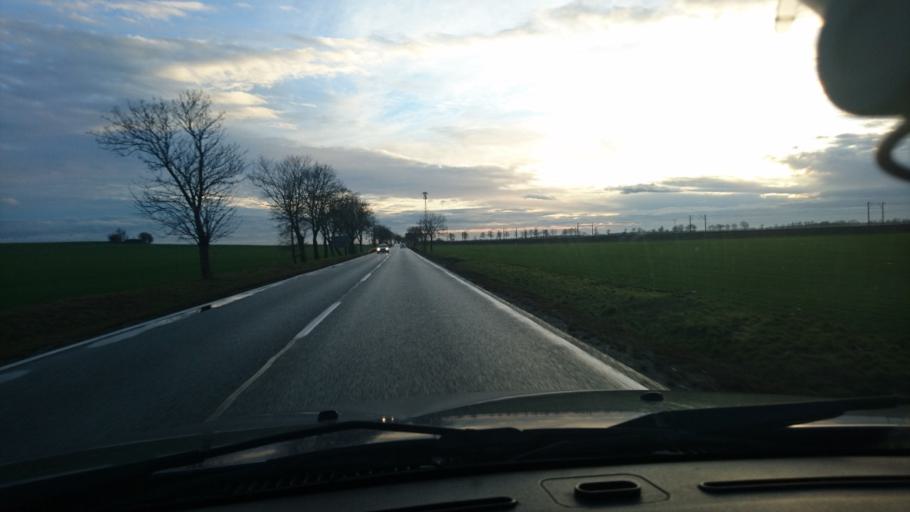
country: PL
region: Opole Voivodeship
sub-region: Powiat kluczborski
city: Byczyna
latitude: 51.1028
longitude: 18.2057
